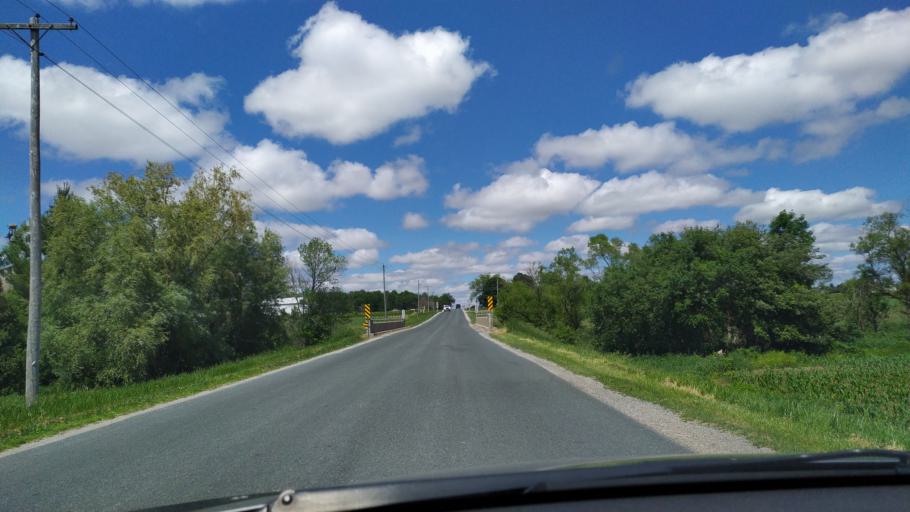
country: CA
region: Ontario
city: Huron East
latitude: 43.4524
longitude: -81.1815
